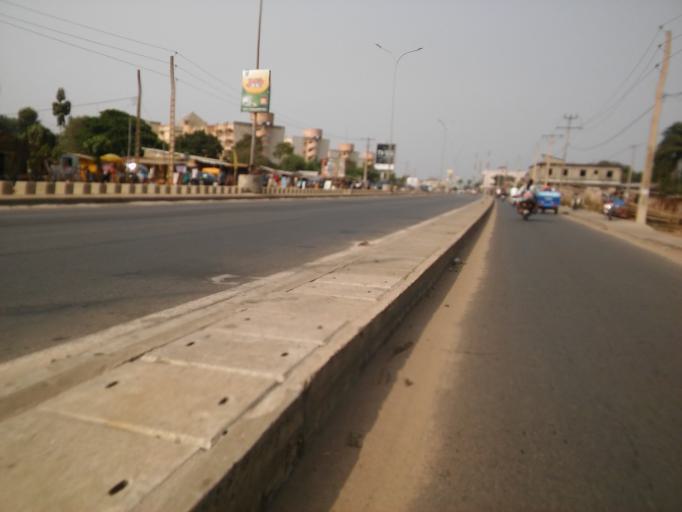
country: BJ
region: Atlantique
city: Abomey-Calavi
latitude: 6.4081
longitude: 2.3434
